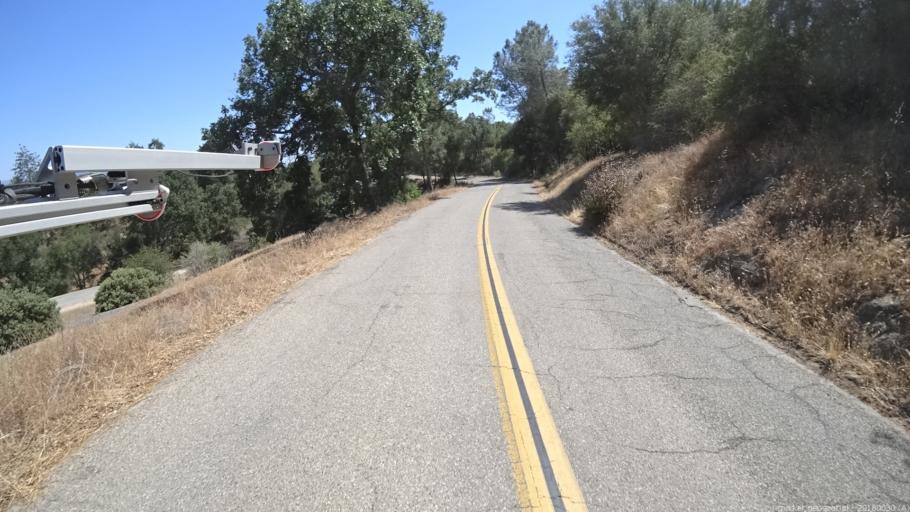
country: US
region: California
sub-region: Fresno County
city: Auberry
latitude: 37.2024
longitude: -119.4987
